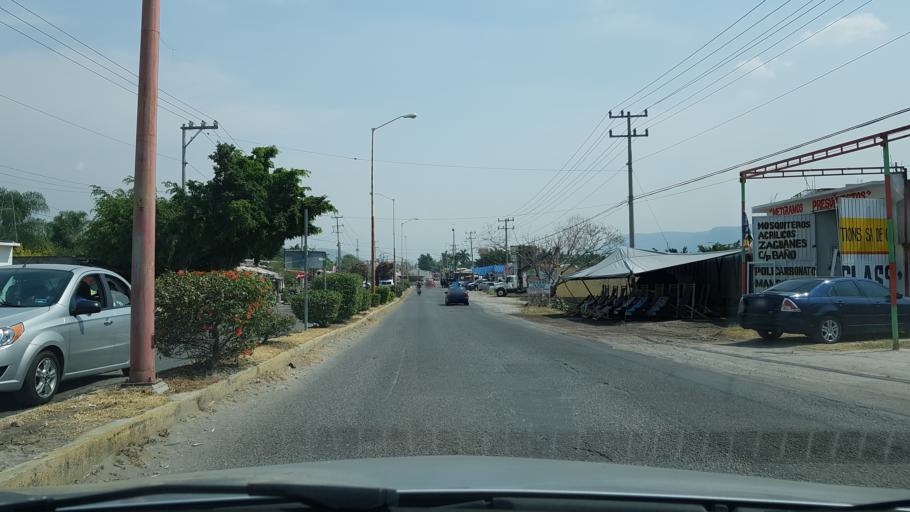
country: MX
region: Morelos
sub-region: Xochitepec
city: Chiconcuac
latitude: 18.7951
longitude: -99.2009
